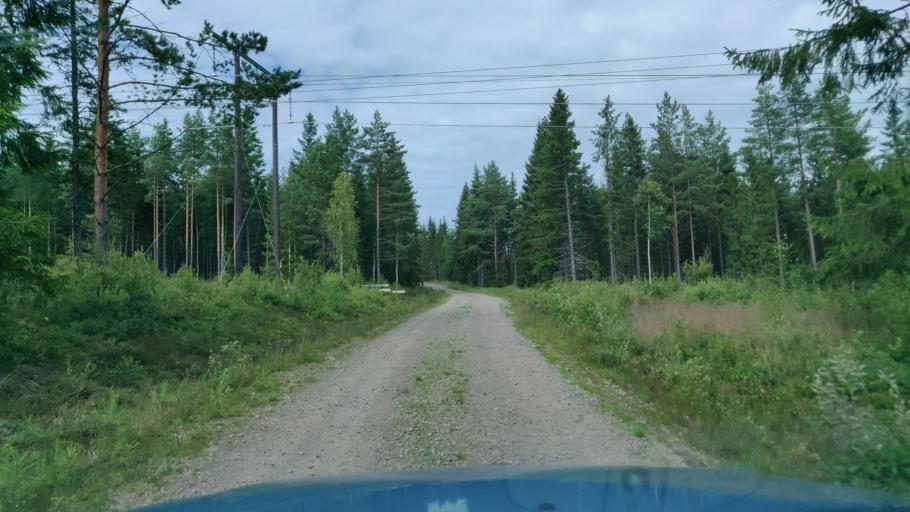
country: SE
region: Vaermland
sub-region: Hagfors Kommun
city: Hagfors
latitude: 59.9438
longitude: 13.5964
